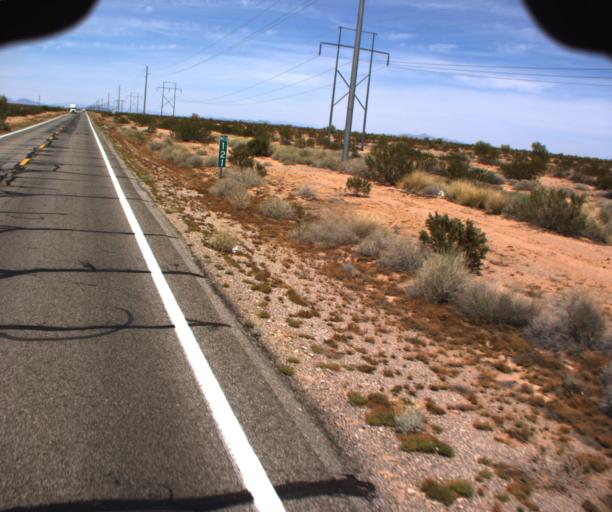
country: US
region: Arizona
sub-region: La Paz County
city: Quartzsite
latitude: 33.8402
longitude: -114.2170
